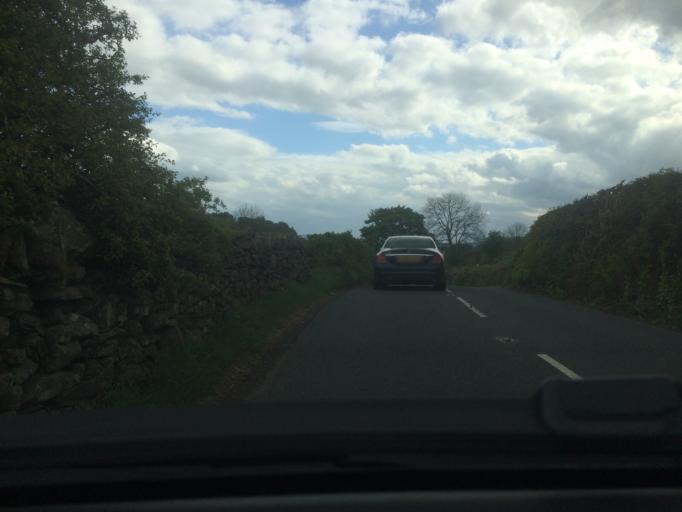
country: GB
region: England
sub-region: Cumbria
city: Windermere
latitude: 54.4239
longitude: -2.9058
